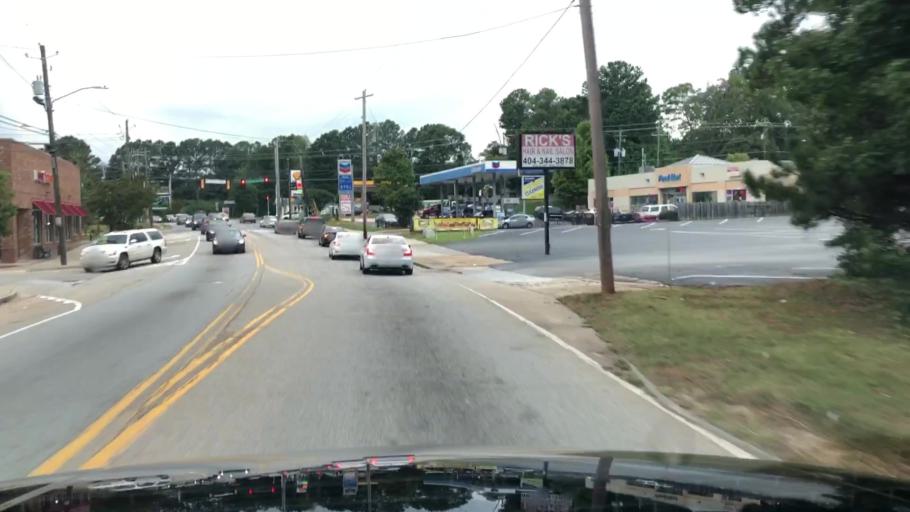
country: US
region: Georgia
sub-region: Fulton County
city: College Park
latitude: 33.6962
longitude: -84.5340
